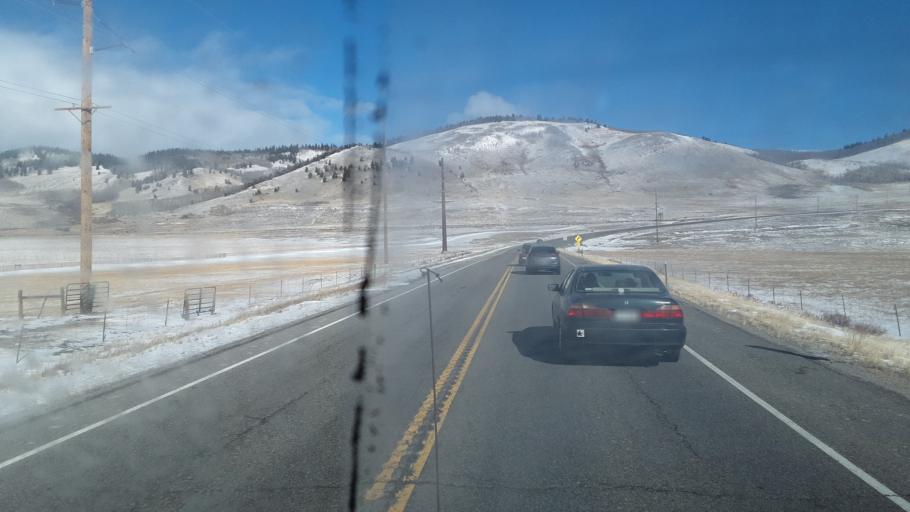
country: US
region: Colorado
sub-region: Summit County
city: Breckenridge
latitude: 39.4024
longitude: -105.7807
